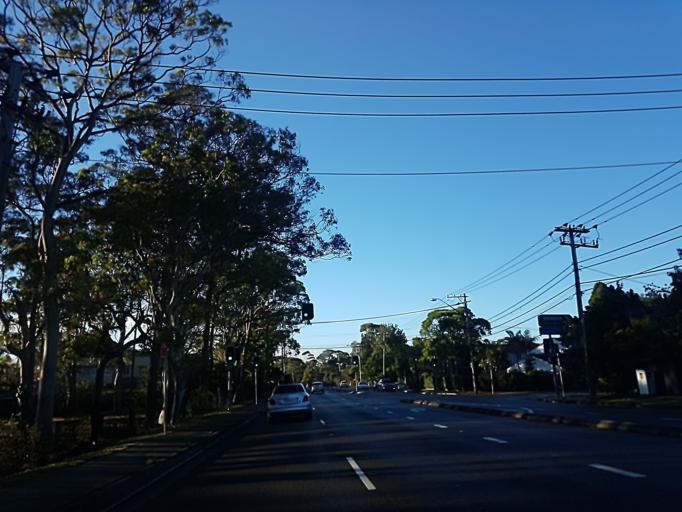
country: AU
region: New South Wales
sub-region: Warringah
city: Davidson
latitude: -33.7383
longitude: 151.2203
